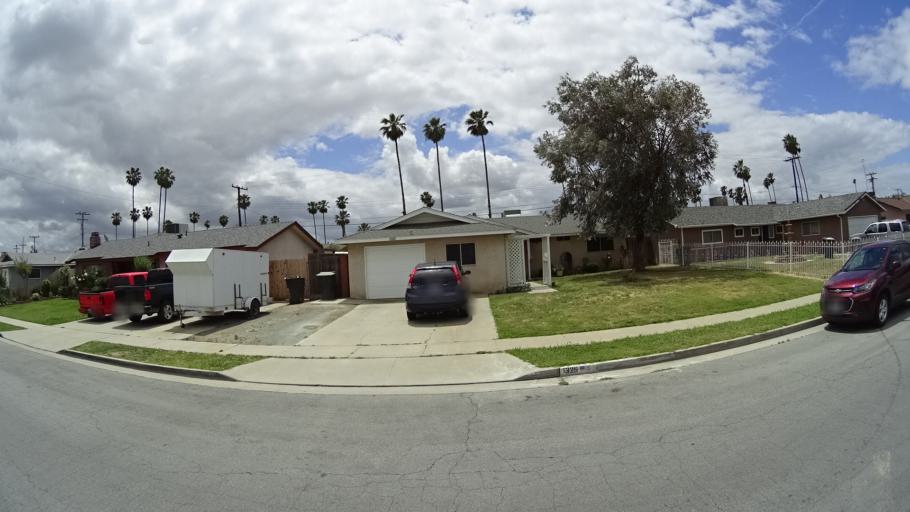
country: US
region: California
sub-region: Kings County
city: Hanford
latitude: 36.3392
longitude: -119.6251
